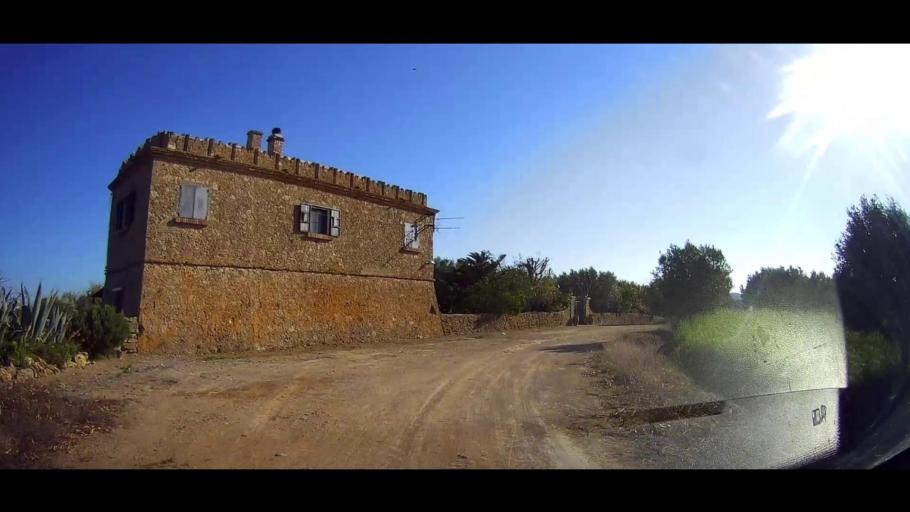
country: IT
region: Calabria
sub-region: Provincia di Crotone
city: Crotone
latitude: 39.0187
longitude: 17.1871
